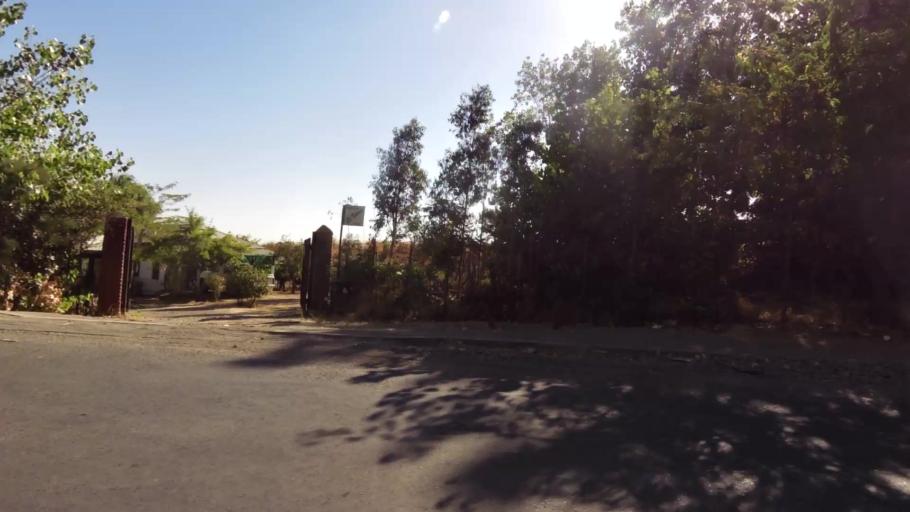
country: CL
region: Maule
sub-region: Provincia de Talca
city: Talca
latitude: -35.4498
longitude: -71.6466
